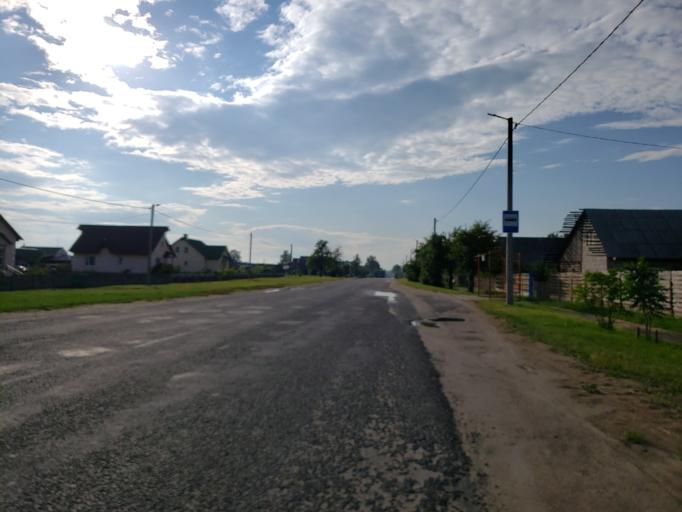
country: BY
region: Minsk
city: Chervyen'
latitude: 53.7006
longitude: 28.4454
